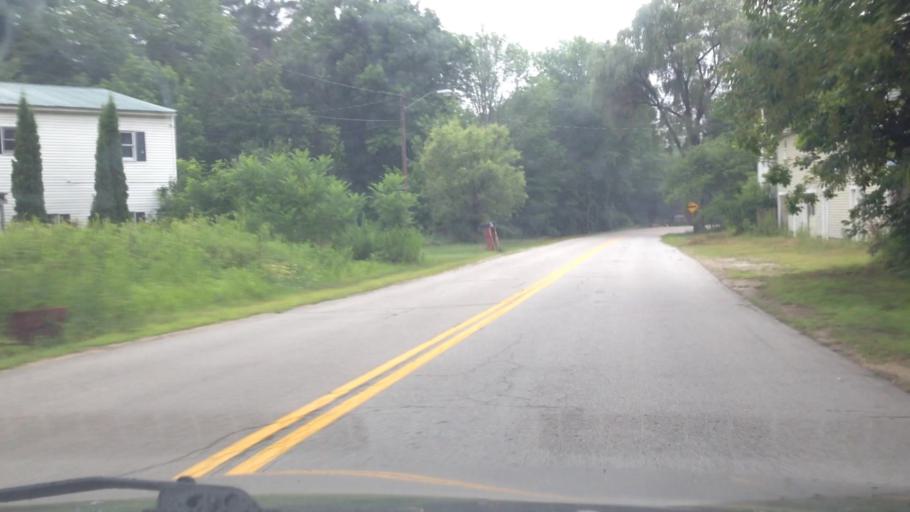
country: US
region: New Hampshire
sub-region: Cheshire County
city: Swanzey
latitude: 42.8504
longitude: -72.2589
